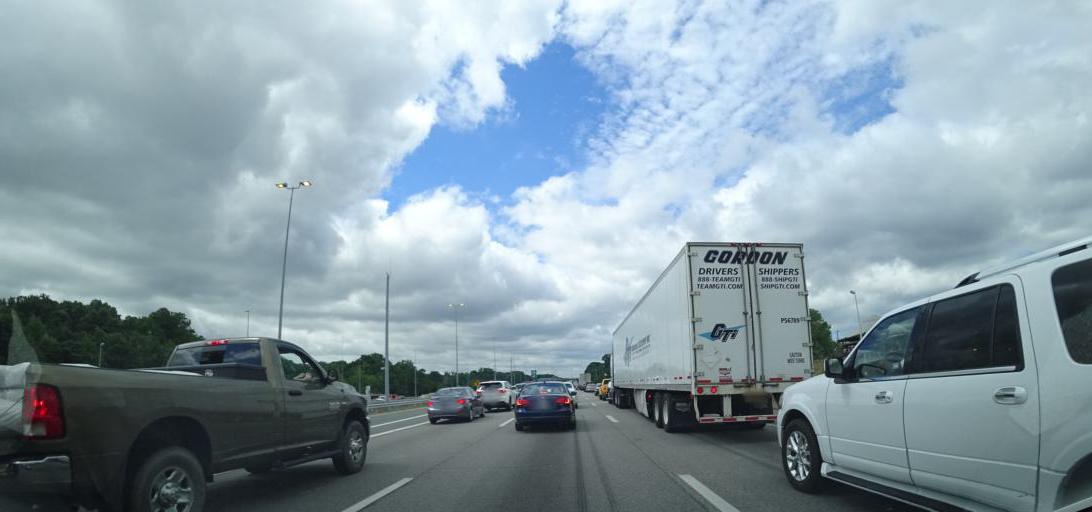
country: US
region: Virginia
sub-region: Prince William County
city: Potomac Mills
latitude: 38.6359
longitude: -77.2905
